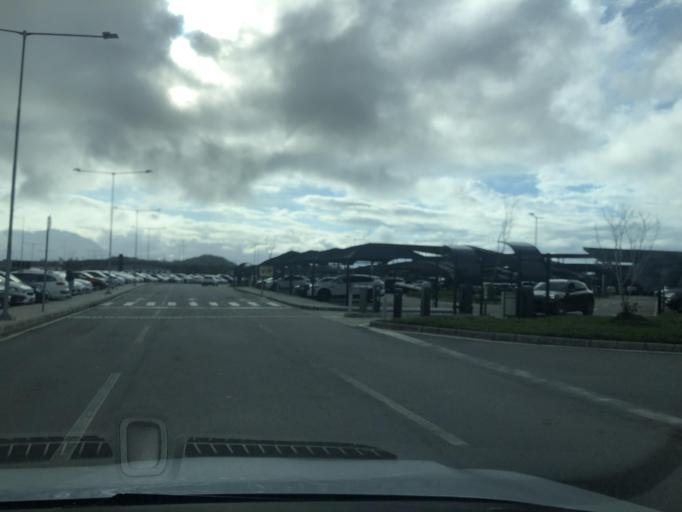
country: BR
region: Santa Catarina
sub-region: Florianopolis
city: Tapera
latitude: -27.6752
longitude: -48.5443
